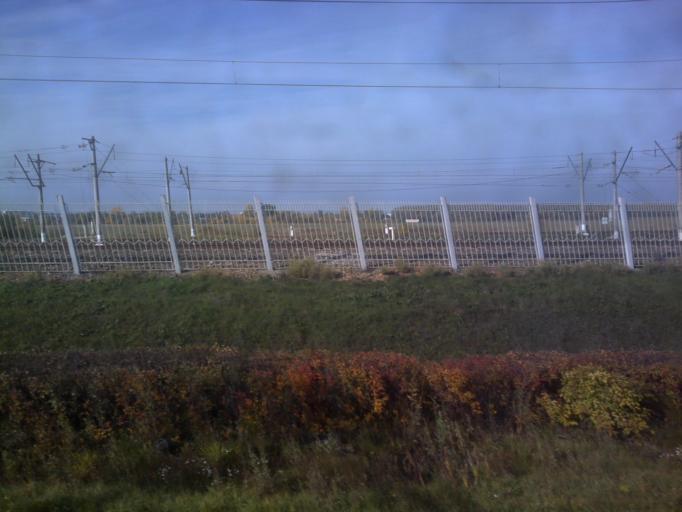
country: RU
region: Moskovskaya
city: Shcherbinka
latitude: 55.5202
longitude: 37.5649
